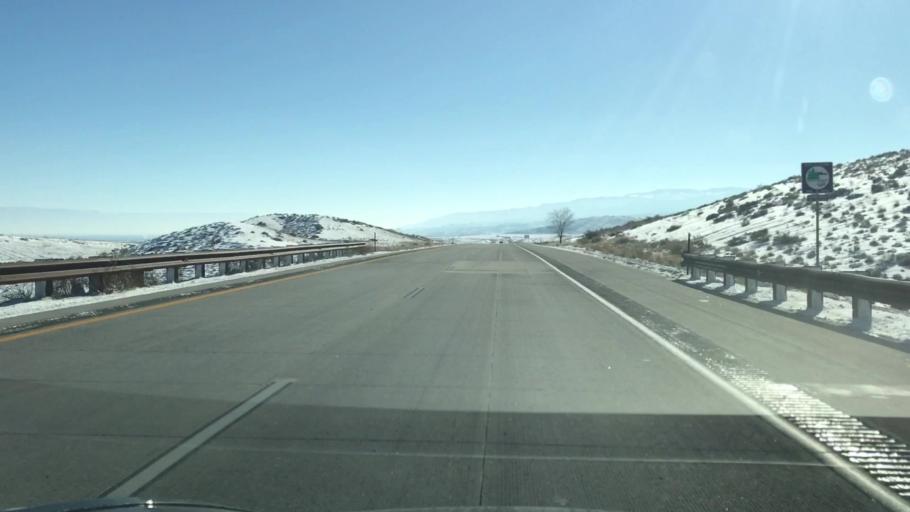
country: US
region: Colorado
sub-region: Mesa County
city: Loma
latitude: 39.1929
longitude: -108.8429
